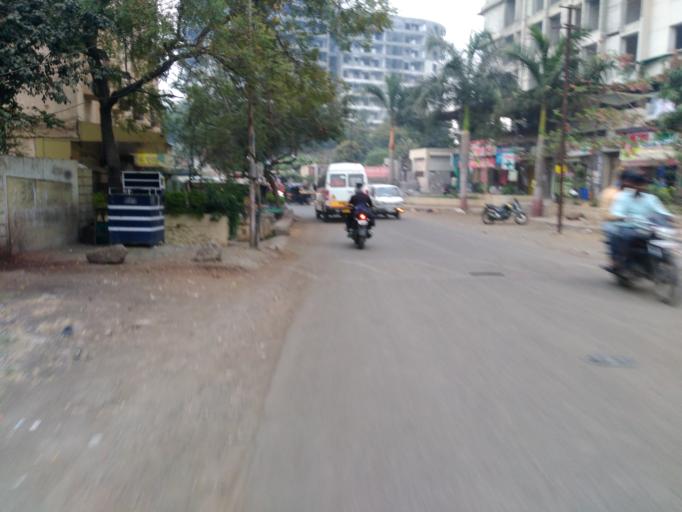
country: IN
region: Maharashtra
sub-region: Pune Division
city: Pune
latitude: 18.4595
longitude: 73.8884
